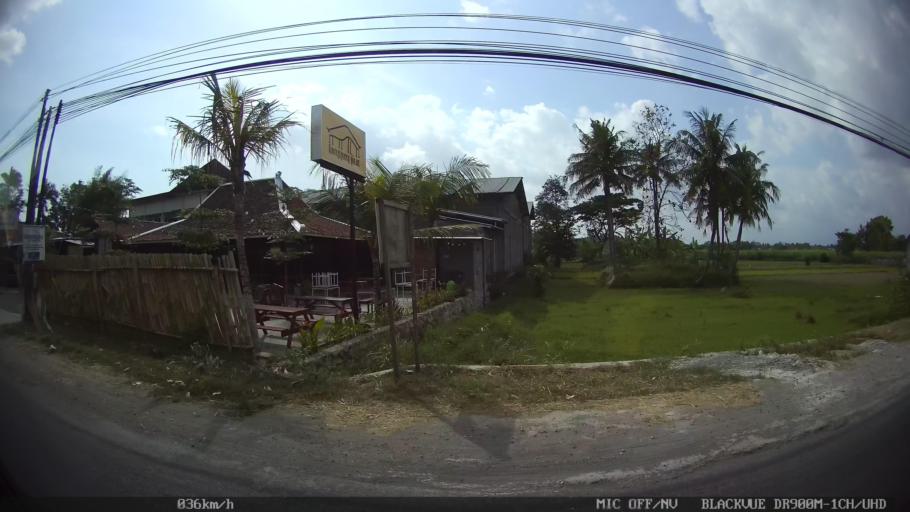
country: ID
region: Daerah Istimewa Yogyakarta
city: Kasihan
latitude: -7.8299
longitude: 110.3185
